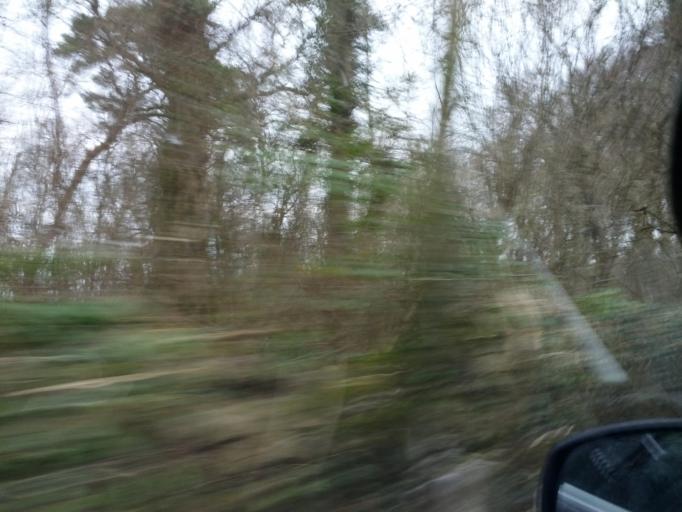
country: IE
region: Connaught
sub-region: County Galway
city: Oranmore
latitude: 53.1791
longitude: -8.9009
